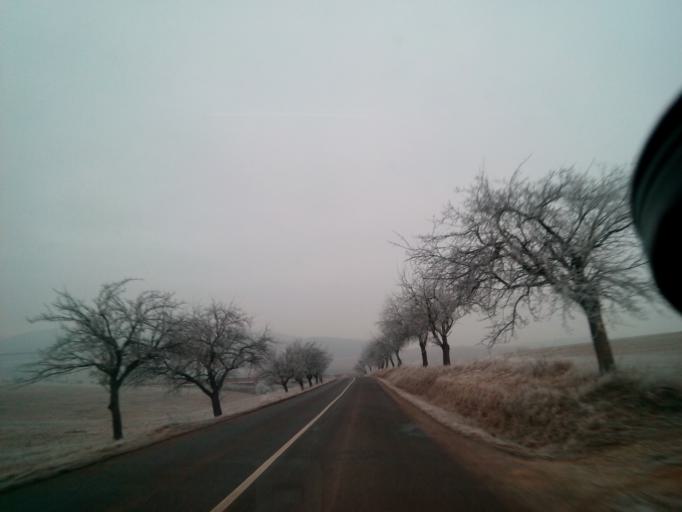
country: SK
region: Presovsky
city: Lubica
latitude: 48.9855
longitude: 20.4208
